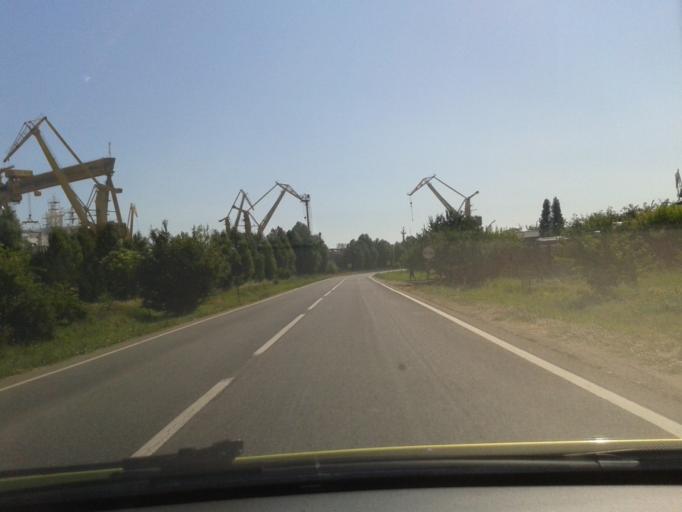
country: RO
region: Constanta
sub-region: Municipiul Mangalia
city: Mangalia
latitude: 43.7943
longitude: 28.5695
